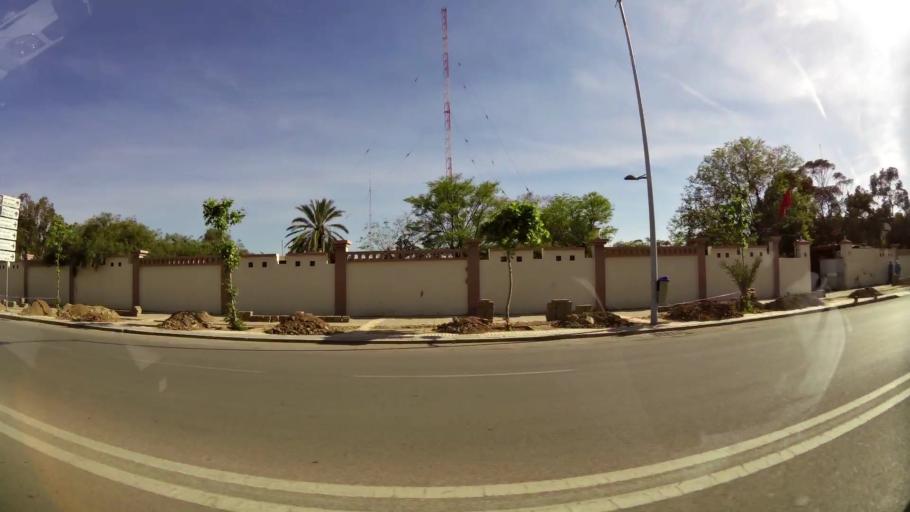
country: MA
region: Oriental
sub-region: Oujda-Angad
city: Oujda
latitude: 34.6643
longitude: -1.9077
